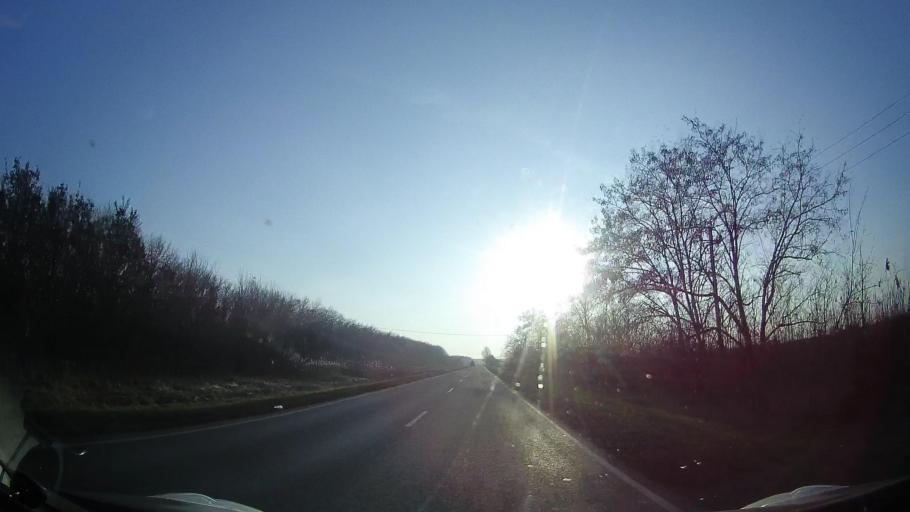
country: RU
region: Rostov
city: Ol'ginskaya
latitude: 47.1498
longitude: 39.9111
